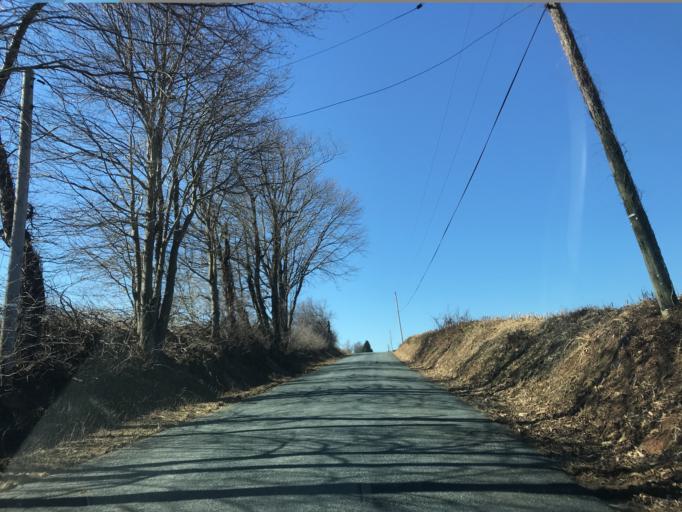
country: US
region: Pennsylvania
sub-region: York County
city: Stewartstown
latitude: 39.7115
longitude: -76.5282
